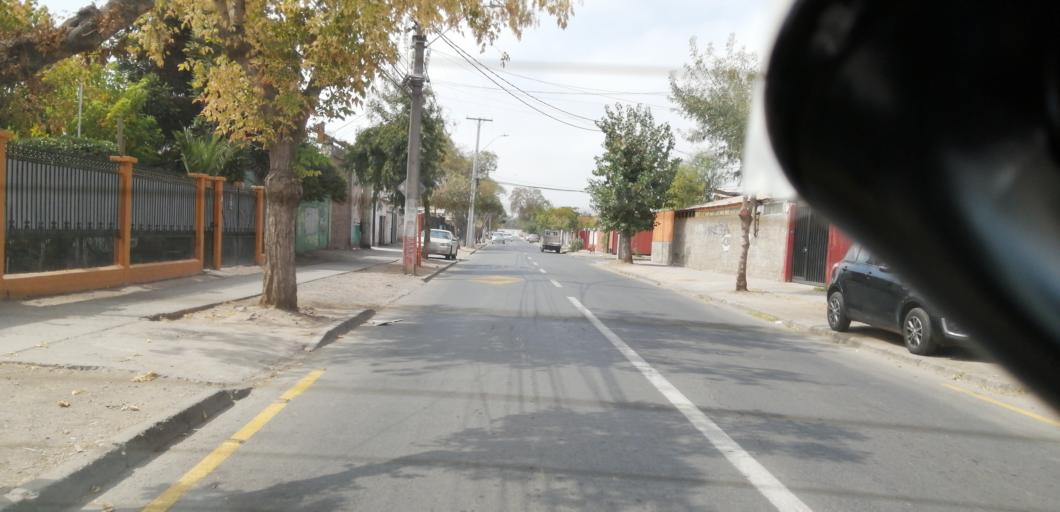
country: CL
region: Santiago Metropolitan
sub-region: Provincia de Santiago
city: Lo Prado
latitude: -33.4419
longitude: -70.7516
